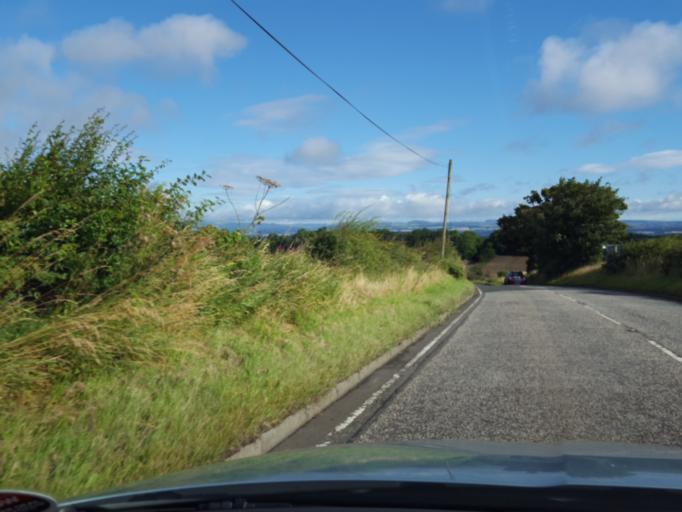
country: GB
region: Scotland
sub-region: West Lothian
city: Broxburn
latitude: 55.9552
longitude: -3.5094
